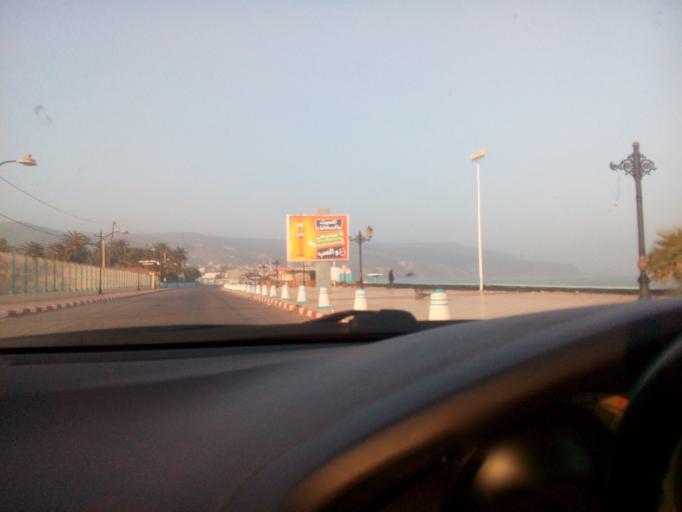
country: DZ
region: Oran
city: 'Ain el Turk
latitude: 35.7059
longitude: -0.8883
